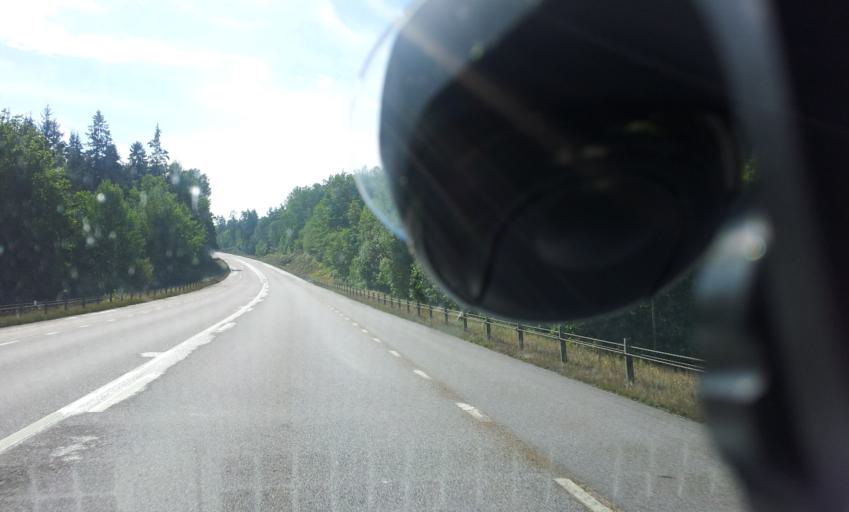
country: SE
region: Kalmar
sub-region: Vasterviks Kommun
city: Ankarsrum
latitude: 57.5622
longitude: 16.4771
